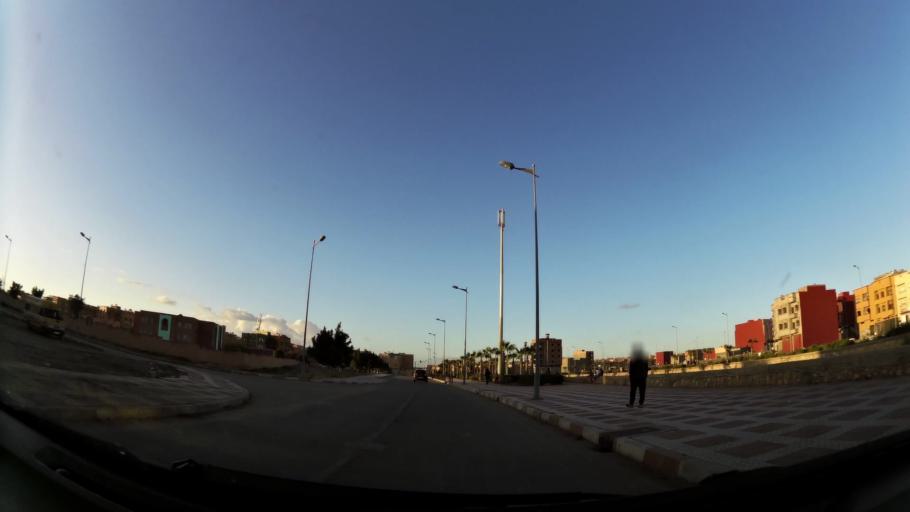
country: MA
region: Marrakech-Tensift-Al Haouz
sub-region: Kelaa-Des-Sraghna
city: Sidi Abdallah
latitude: 32.2376
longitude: -7.9501
